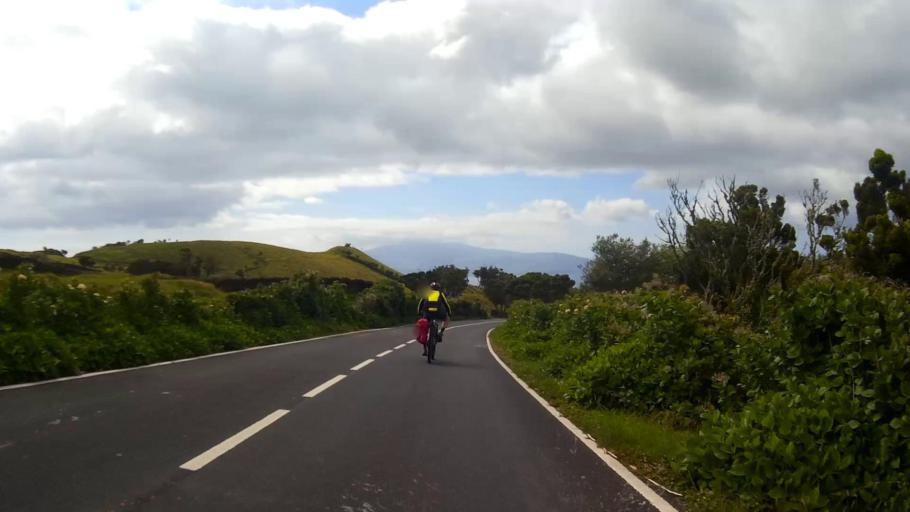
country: PT
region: Azores
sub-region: Madalena
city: Madalena
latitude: 38.4965
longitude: -28.4598
